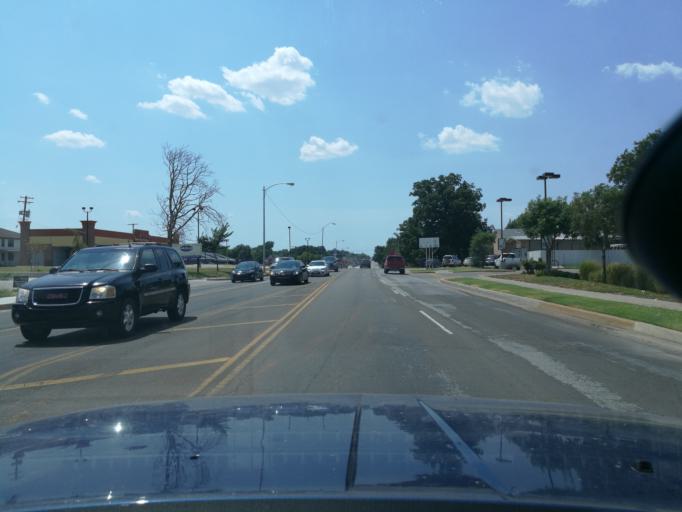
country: US
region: Oklahoma
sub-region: Oklahoma County
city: Oklahoma City
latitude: 35.4208
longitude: -97.5088
